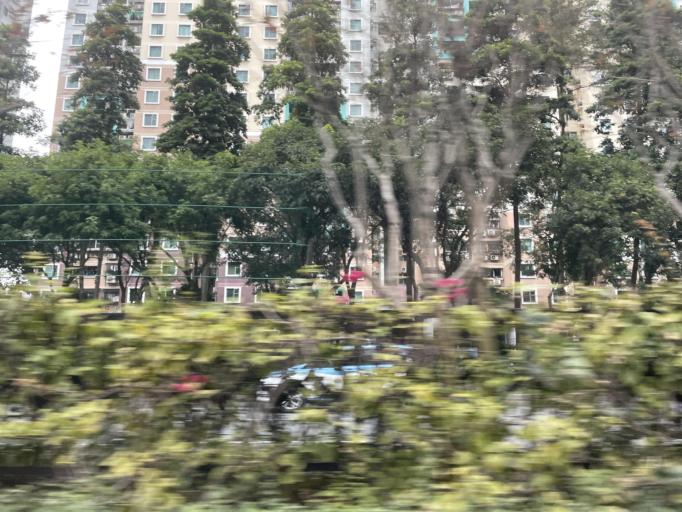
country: CN
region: Guangdong
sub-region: Shenzhen
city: Shenzhen
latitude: 22.5200
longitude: 114.0440
